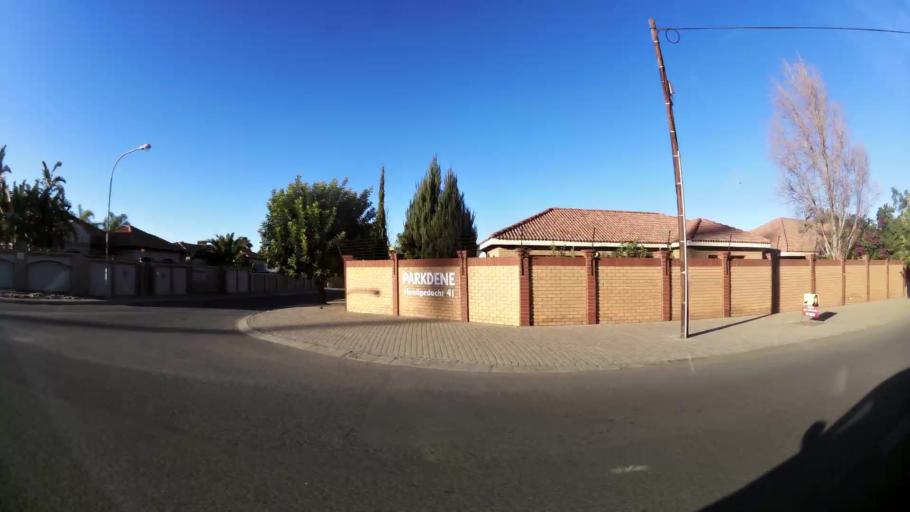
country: ZA
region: Northern Cape
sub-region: Frances Baard District Municipality
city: Kimberley
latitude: -28.7565
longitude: 24.7571
